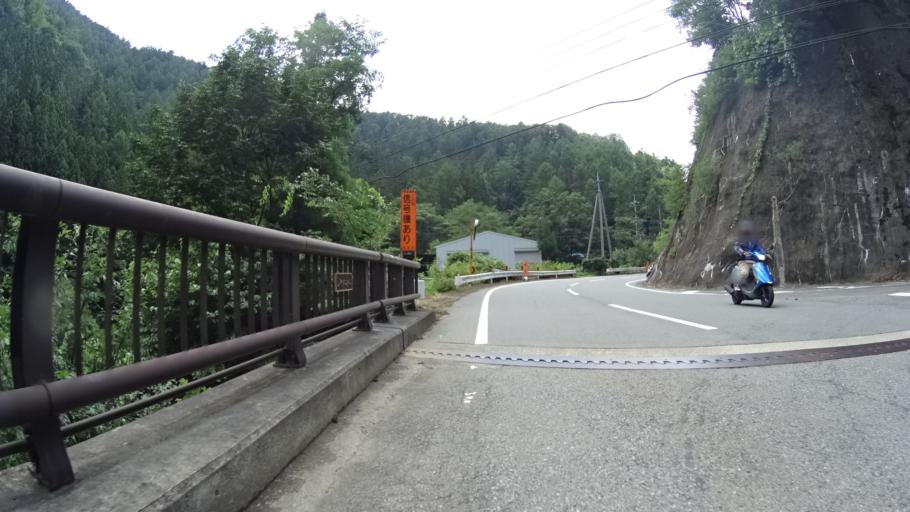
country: JP
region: Gunma
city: Tomioka
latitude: 36.0754
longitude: 138.7076
